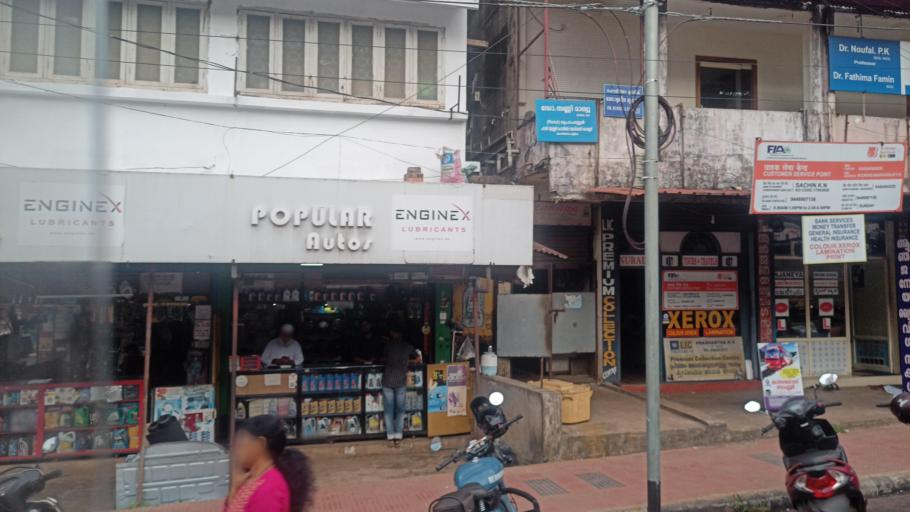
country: IN
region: Kerala
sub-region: Kasaragod District
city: Kasaragod
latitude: 12.5031
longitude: 74.9927
